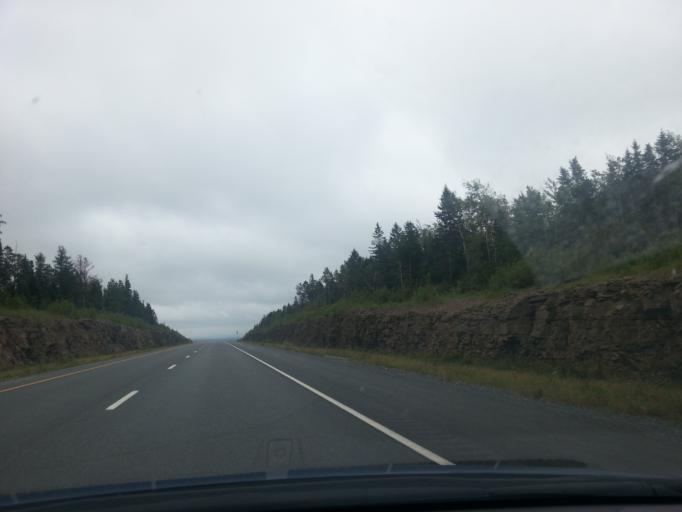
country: CA
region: New Brunswick
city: Nackawic
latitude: 45.9003
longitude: -67.0818
